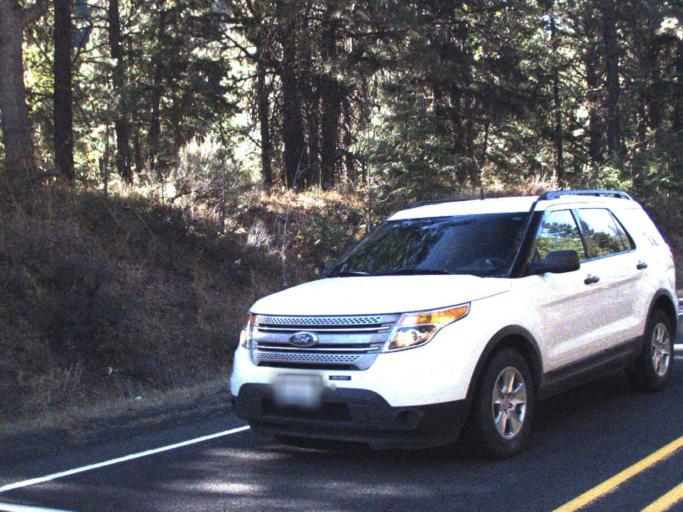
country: US
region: Washington
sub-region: Yakima County
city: Tieton
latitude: 46.6785
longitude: -120.9630
